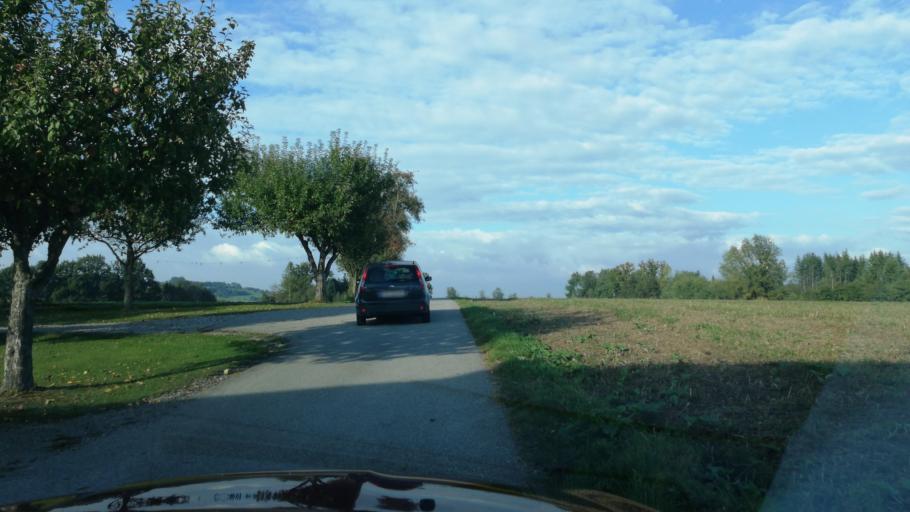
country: AT
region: Upper Austria
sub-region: Politischer Bezirk Grieskirchen
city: Bad Schallerbach
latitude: 48.2233
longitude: 13.9490
